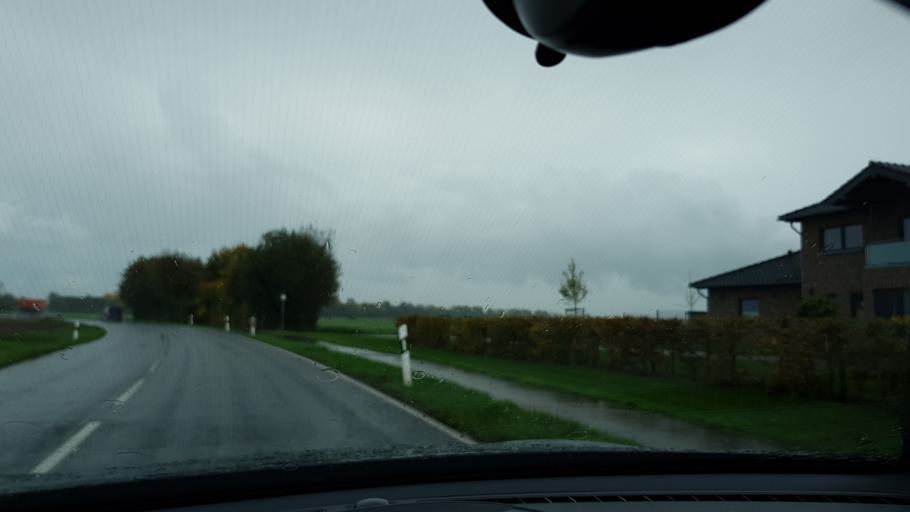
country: DE
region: North Rhine-Westphalia
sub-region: Regierungsbezirk Dusseldorf
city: Rommerskirchen
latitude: 51.0695
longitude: 6.6976
